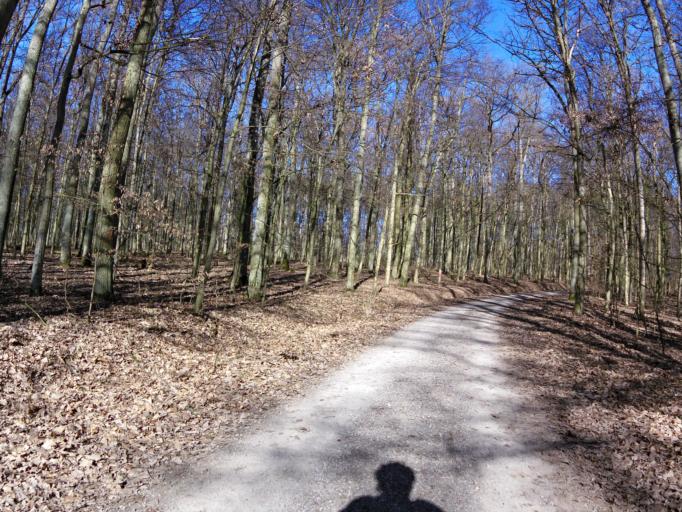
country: DE
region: Bavaria
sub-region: Regierungsbezirk Unterfranken
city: Estenfeld
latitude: 49.8513
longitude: 9.9921
